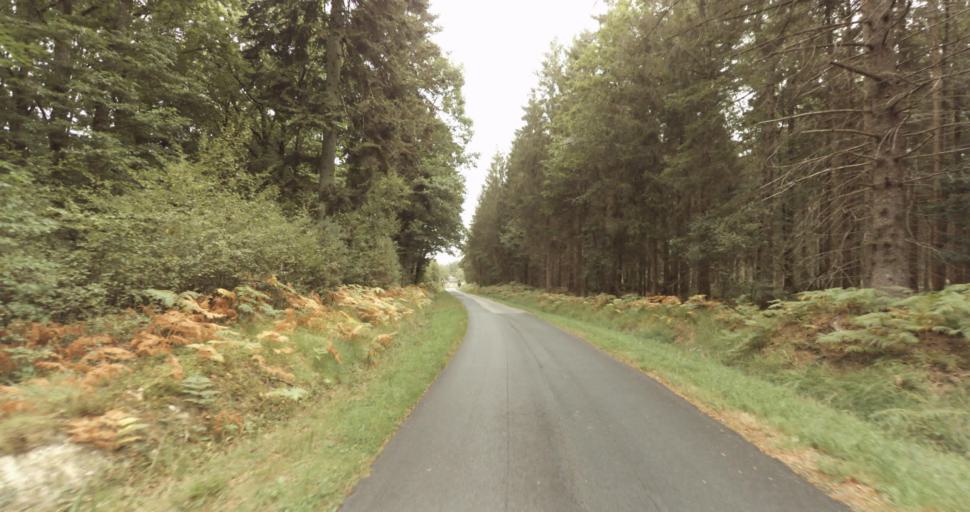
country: FR
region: Lower Normandy
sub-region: Departement de l'Orne
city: Gace
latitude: 48.8294
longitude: 0.3376
